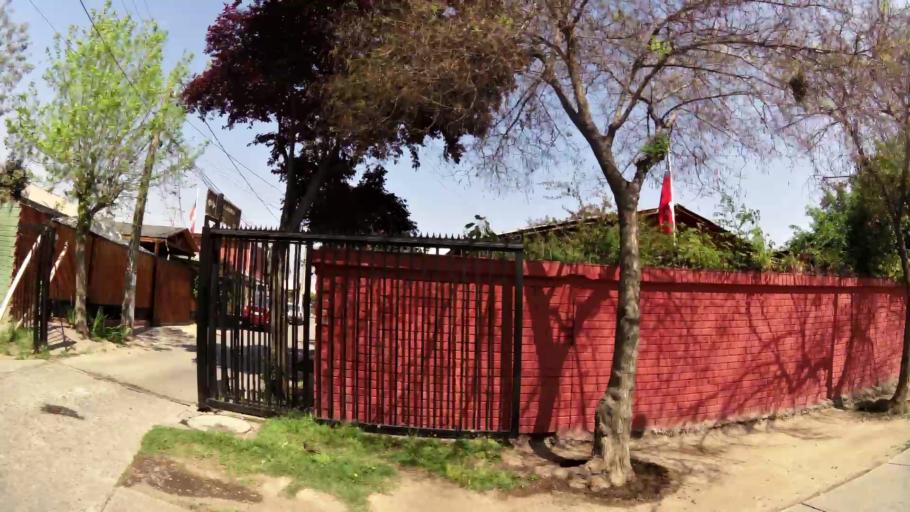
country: CL
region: Santiago Metropolitan
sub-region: Provincia de Santiago
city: La Pintana
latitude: -33.5504
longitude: -70.6033
